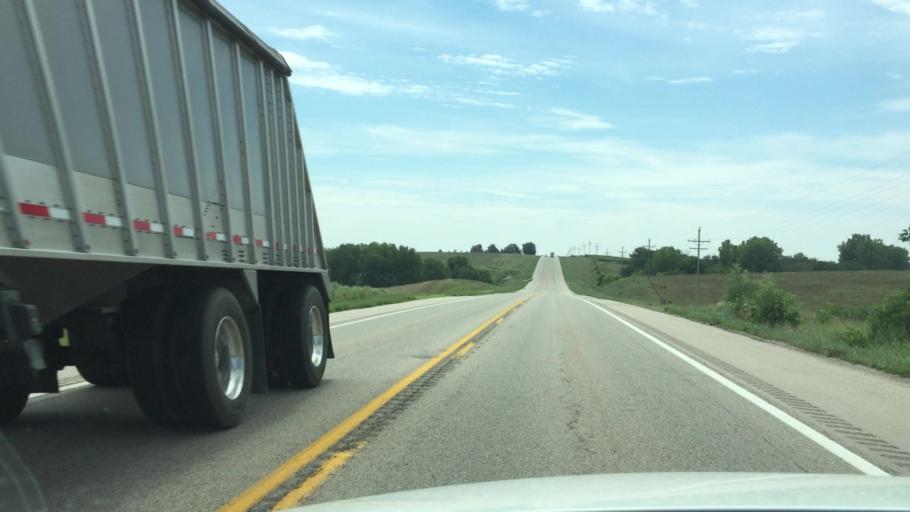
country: US
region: Kansas
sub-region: Nemaha County
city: Sabetha
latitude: 39.7952
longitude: -95.7294
